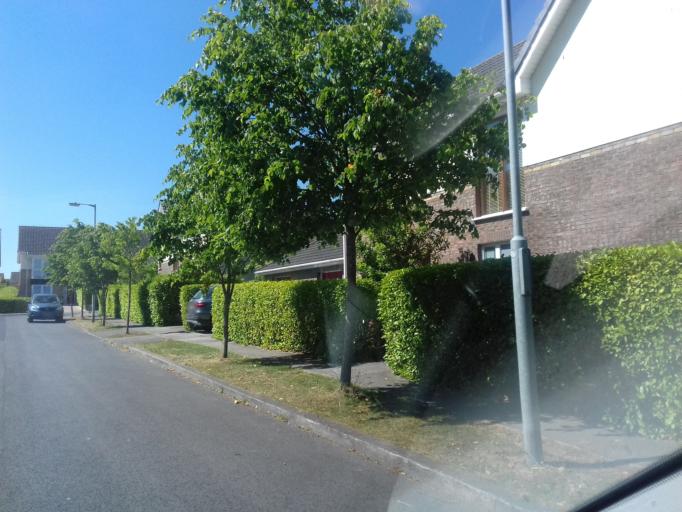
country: IE
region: Leinster
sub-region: Fingal County
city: Swords
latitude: 53.4495
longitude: -6.2468
